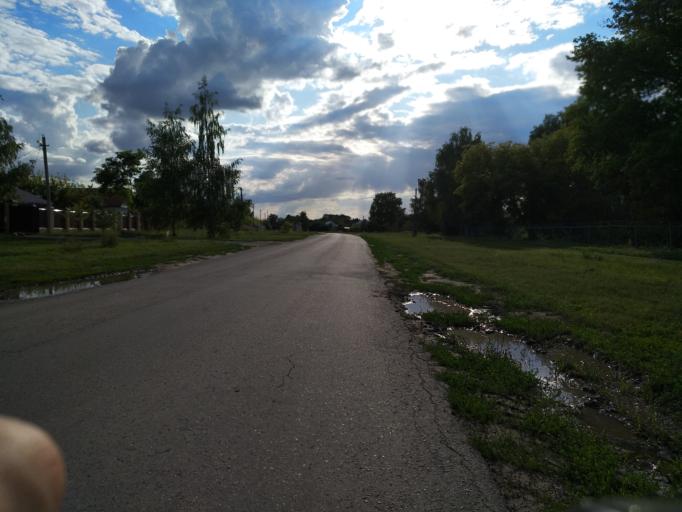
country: RU
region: Lipetsk
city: Dobrinka
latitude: 52.0389
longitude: 40.5374
